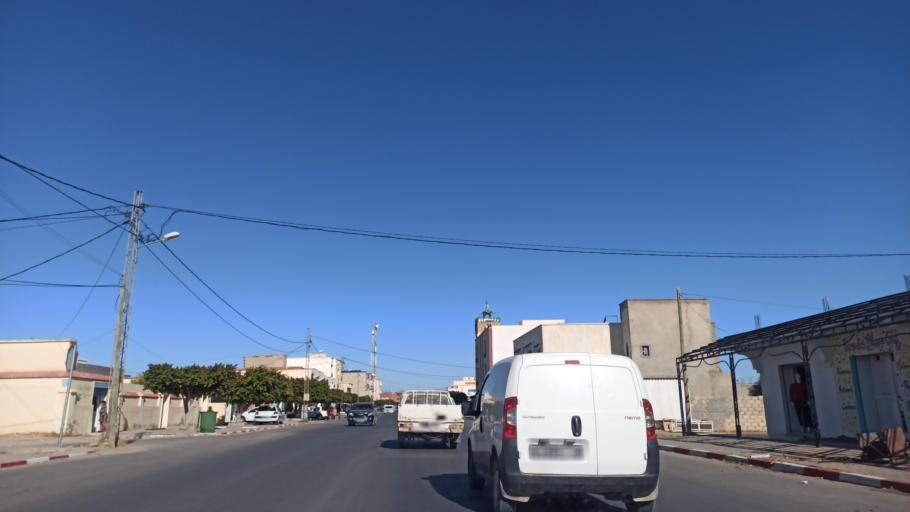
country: TN
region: Sidi Bu Zayd
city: Bi'r al Hufayy
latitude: 34.9247
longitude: 9.1903
